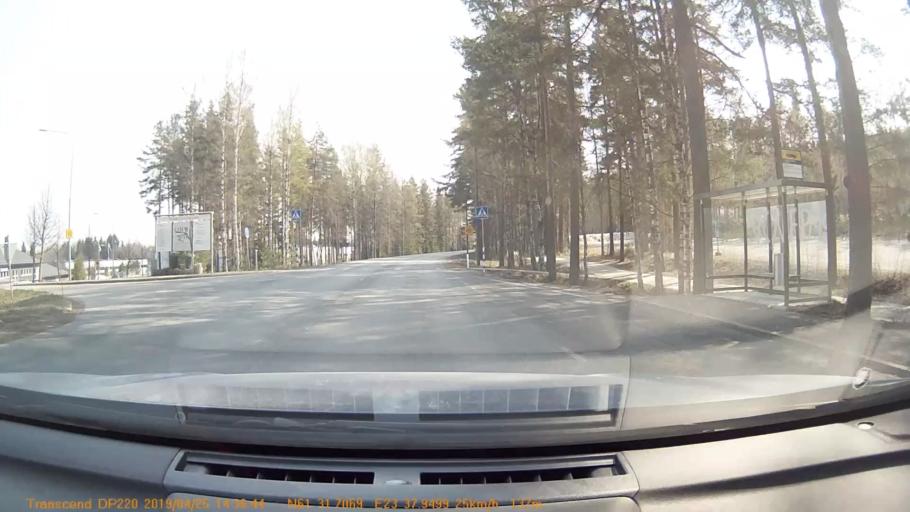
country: FI
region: Pirkanmaa
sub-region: Tampere
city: Yloejaervi
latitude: 61.5285
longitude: 23.6324
